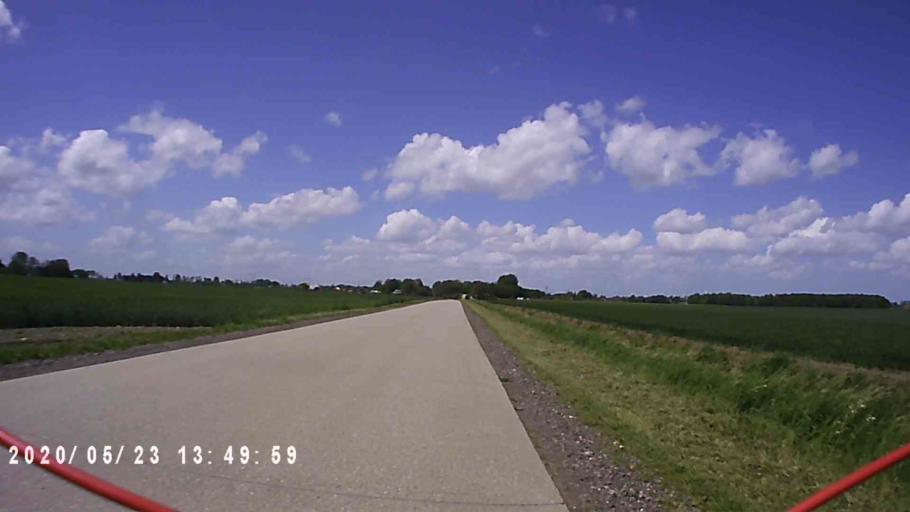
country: NL
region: Groningen
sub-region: Gemeente  Oldambt
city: Winschoten
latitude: 53.2644
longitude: 7.0440
